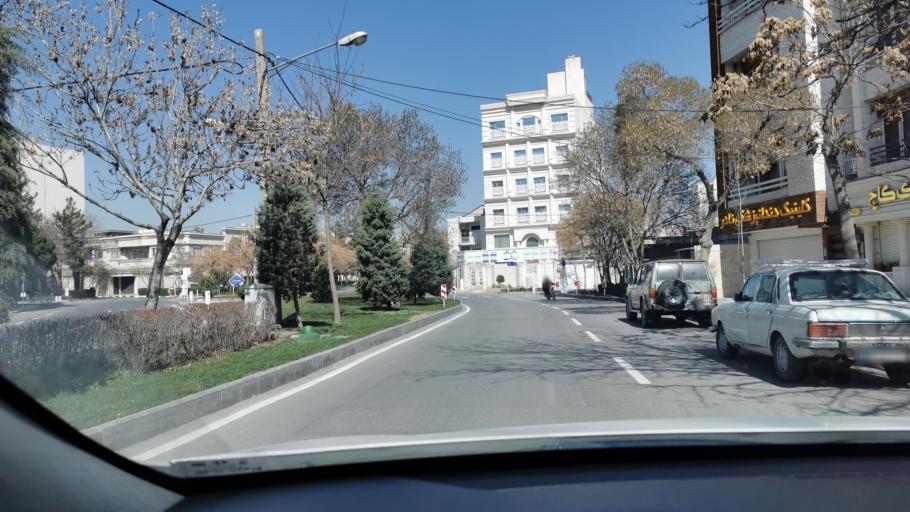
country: IR
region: Razavi Khorasan
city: Mashhad
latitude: 36.2885
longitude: 59.5733
